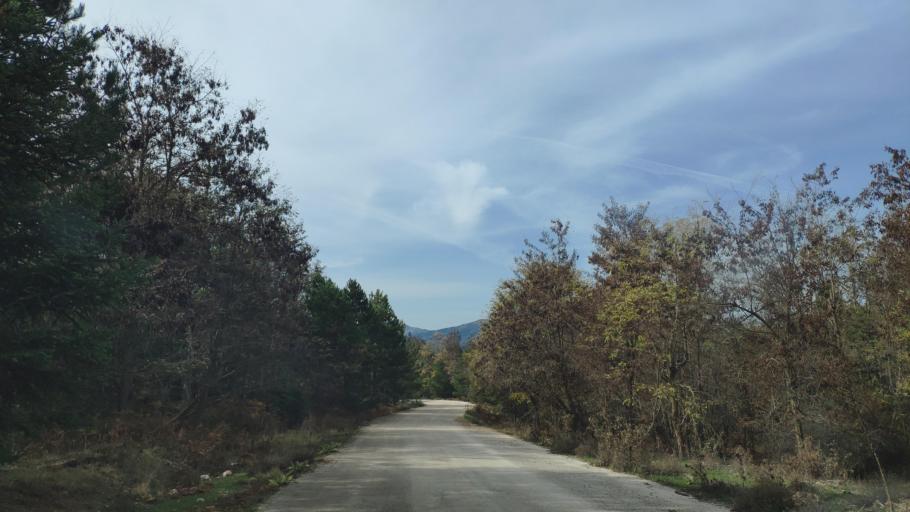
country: GR
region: West Greece
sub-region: Nomos Achaias
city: Aiyira
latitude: 38.0340
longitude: 22.3815
